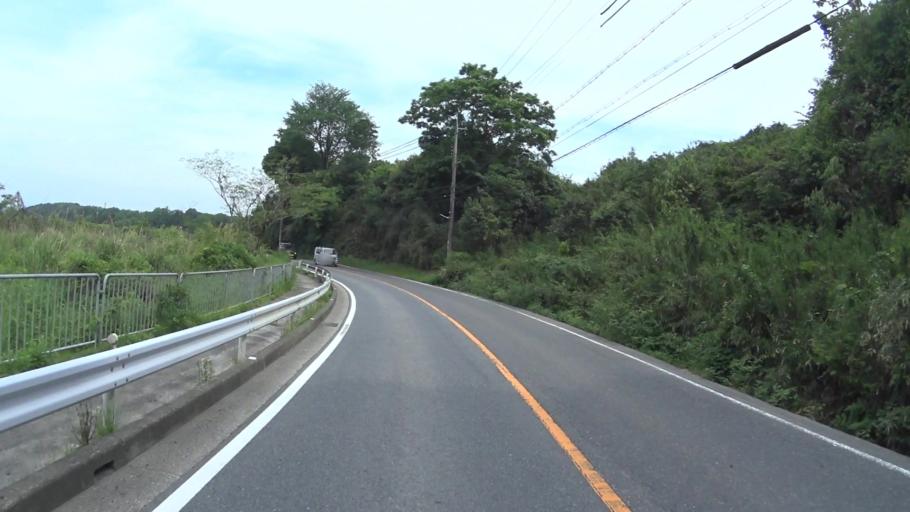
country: JP
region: Shiga Prefecture
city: Kitahama
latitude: 35.1589
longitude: 135.8669
